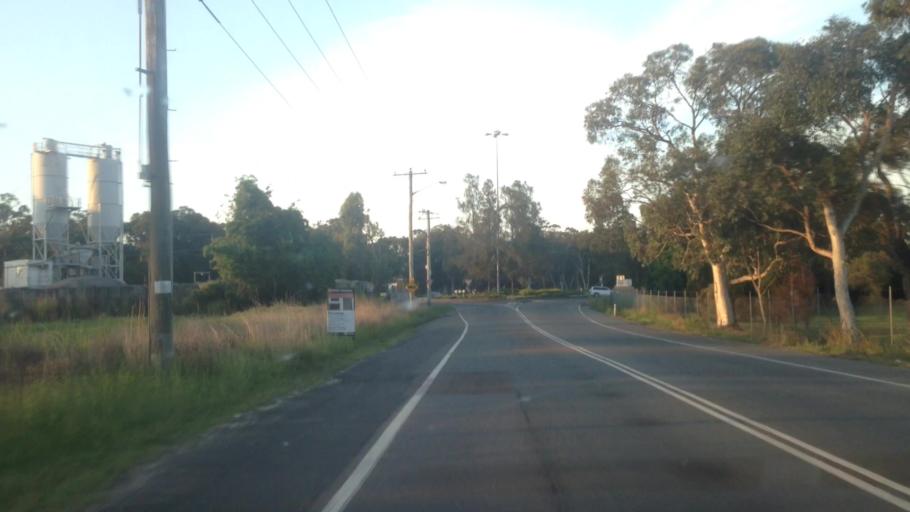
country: AU
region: New South Wales
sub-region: Lake Macquarie Shire
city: Dora Creek
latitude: -33.1142
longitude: 151.4782
